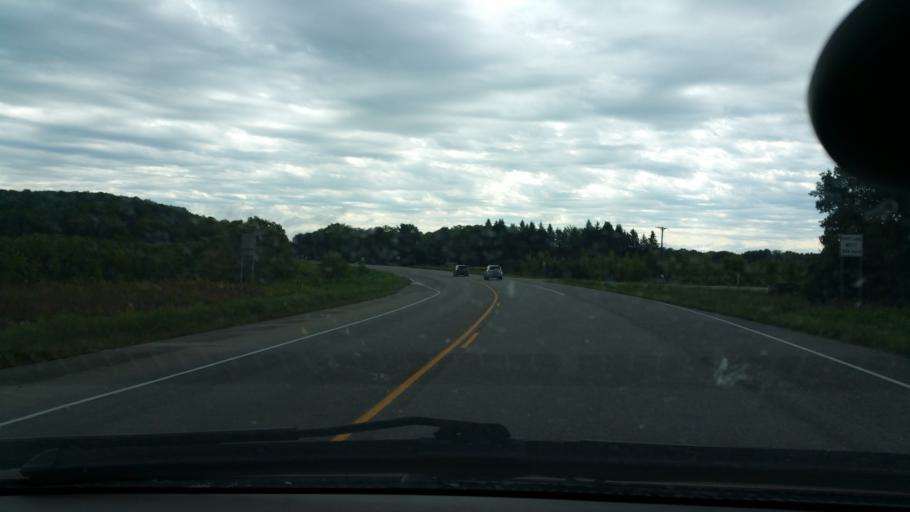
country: US
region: Minnesota
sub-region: Rice County
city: Dundas
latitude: 44.4575
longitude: -93.1955
